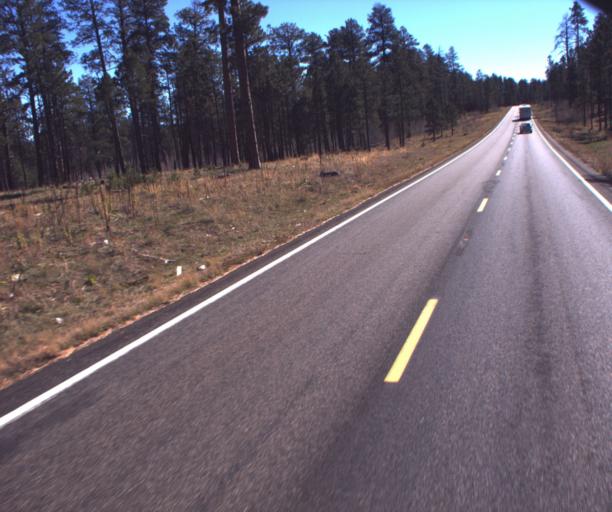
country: US
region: Arizona
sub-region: Coconino County
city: Fredonia
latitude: 36.6822
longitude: -112.2152
